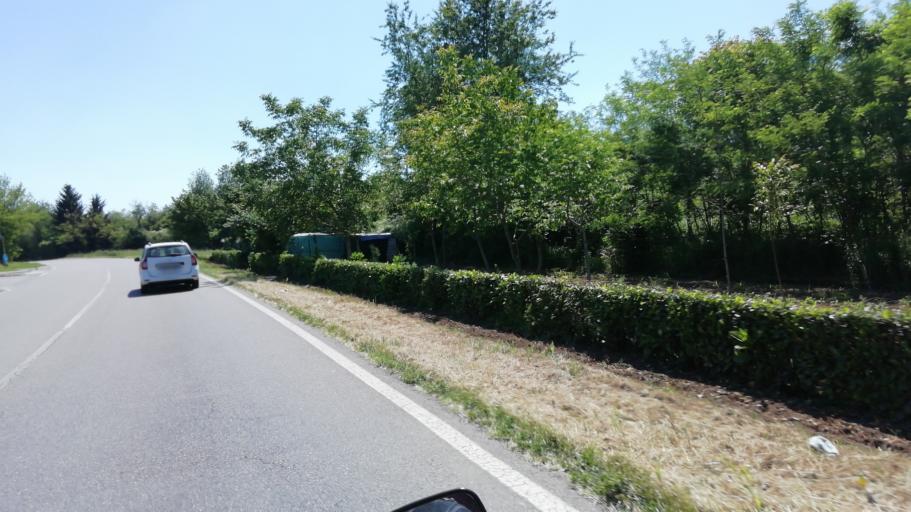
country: IT
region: Lombardy
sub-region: Provincia di Varese
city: Lonate Pozzolo
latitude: 45.6006
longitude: 8.7432
